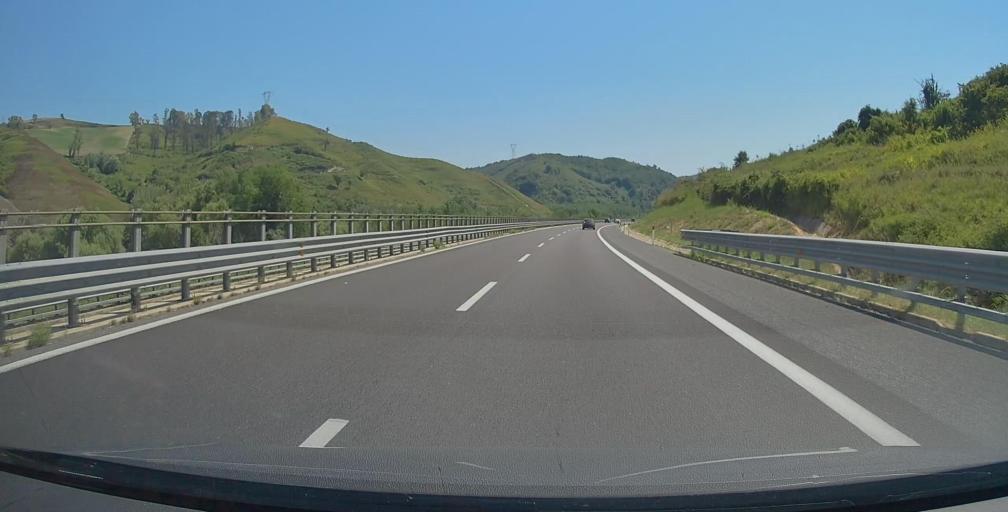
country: IT
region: Calabria
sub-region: Provincia di Vibo-Valentia
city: Francica
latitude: 38.5874
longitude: 16.1357
